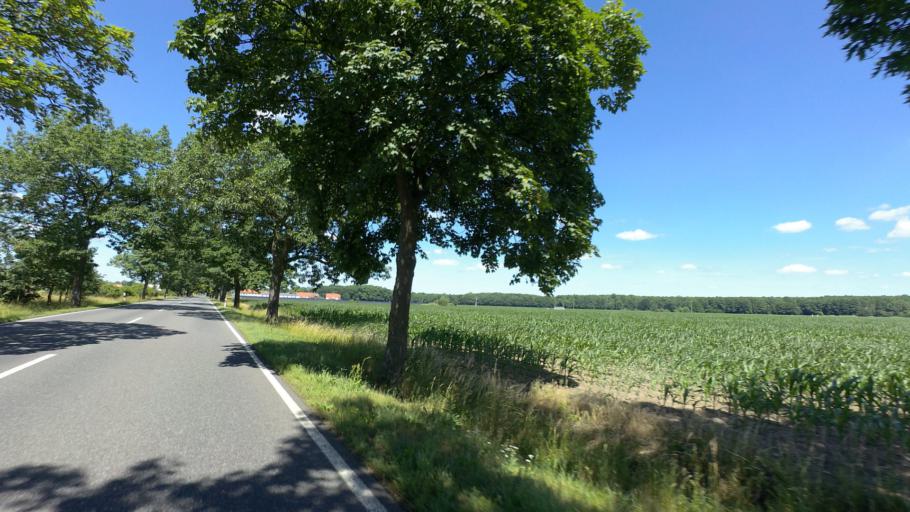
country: DE
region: Brandenburg
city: Kasel-Golzig
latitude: 51.9430
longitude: 13.6525
